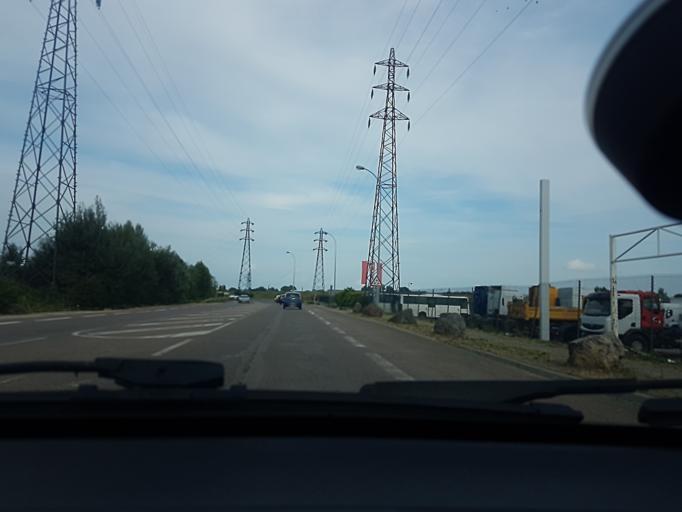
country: FR
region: Bourgogne
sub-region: Departement de Saone-et-Loire
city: Saint-Marcel
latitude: 46.7725
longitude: 4.8699
